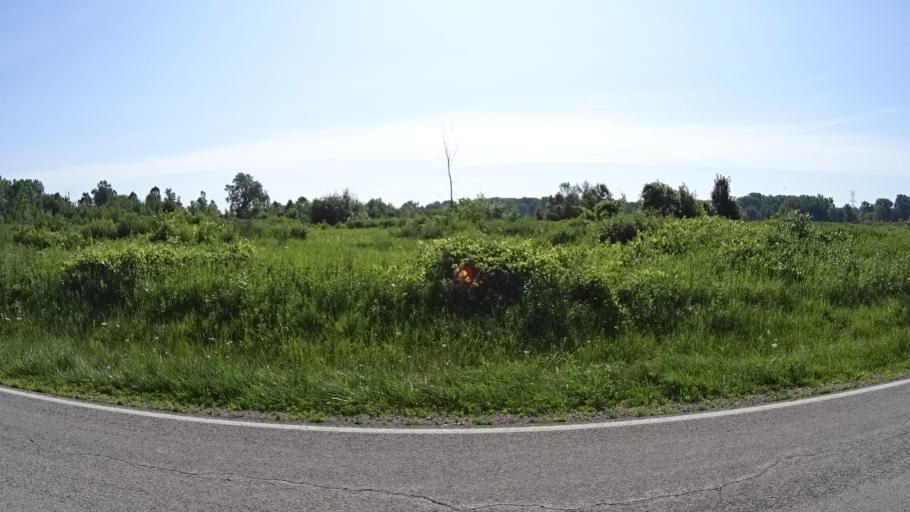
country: US
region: Ohio
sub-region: Huron County
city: Bellevue
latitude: 41.3931
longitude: -82.8460
